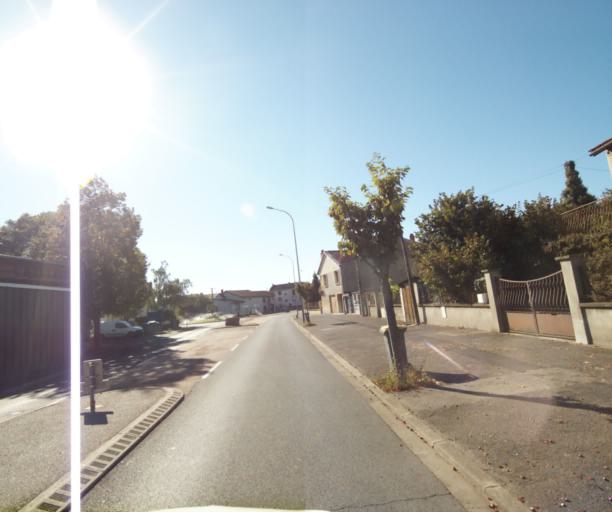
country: FR
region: Auvergne
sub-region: Departement du Puy-de-Dome
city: Gerzat
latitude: 45.8241
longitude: 3.1419
